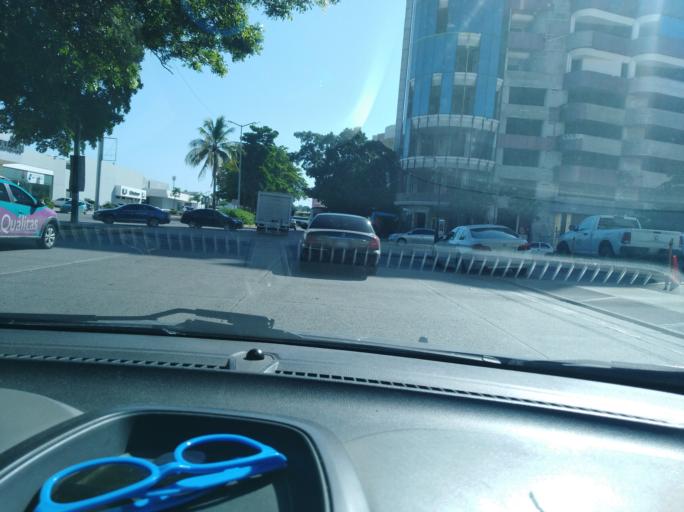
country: MX
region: Sinaloa
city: Culiacan
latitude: 24.7949
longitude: -107.4123
